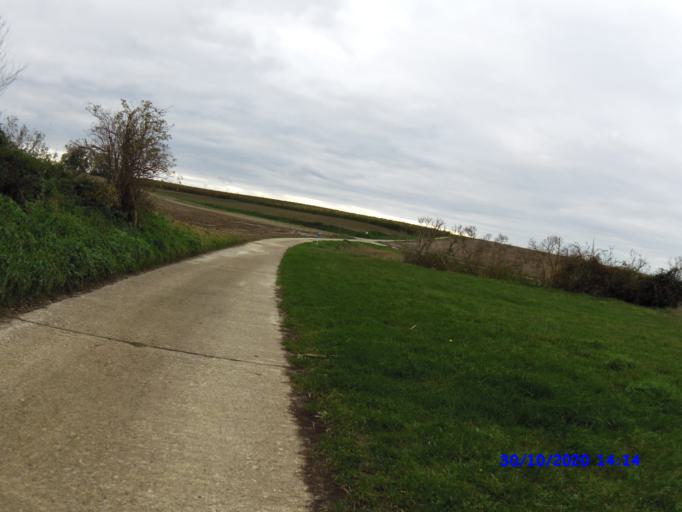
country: BE
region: Flanders
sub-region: Provincie Limburg
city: Gingelom
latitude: 50.7412
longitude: 5.1675
